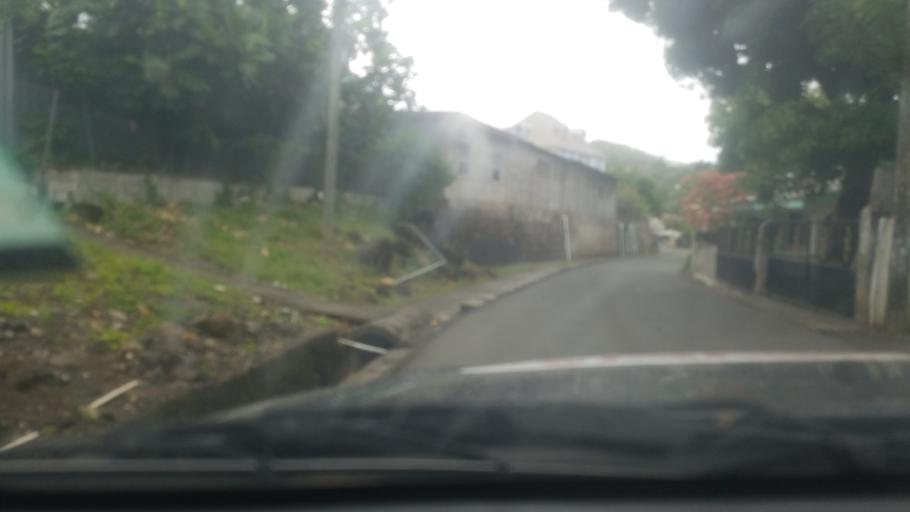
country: LC
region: Laborie Quarter
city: Laborie
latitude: 13.7523
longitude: -60.9971
